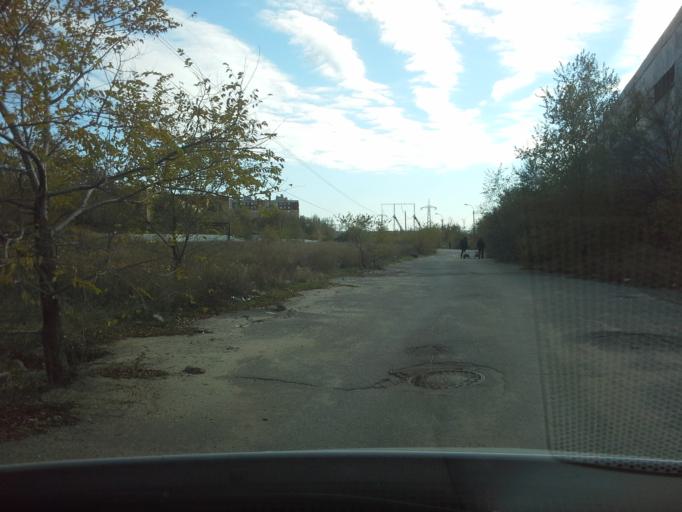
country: RU
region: Volgograd
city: Vodstroy
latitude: 48.8373
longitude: 44.6306
